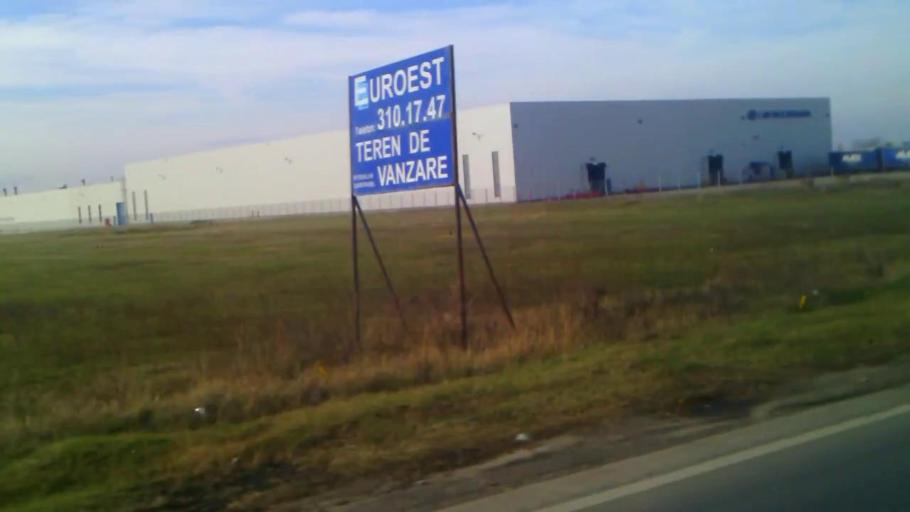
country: RO
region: Ilfov
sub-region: Comuna Berceni
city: Berceni
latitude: 44.3446
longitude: 26.1616
